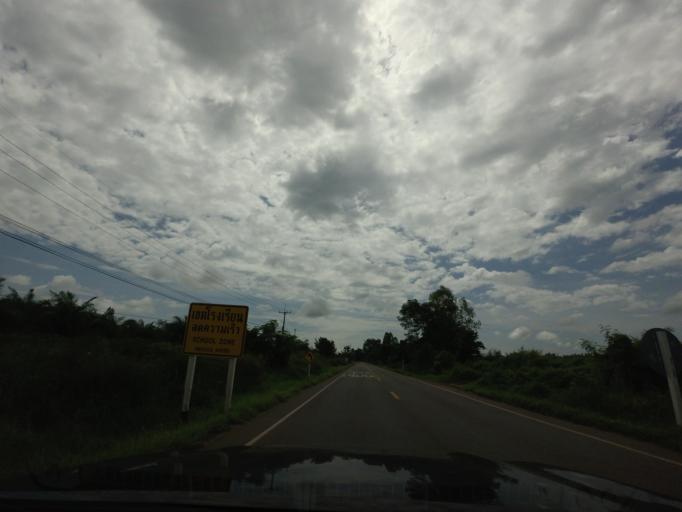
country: TH
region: Changwat Udon Thani
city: Nam Som
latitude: 17.8083
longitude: 102.2716
